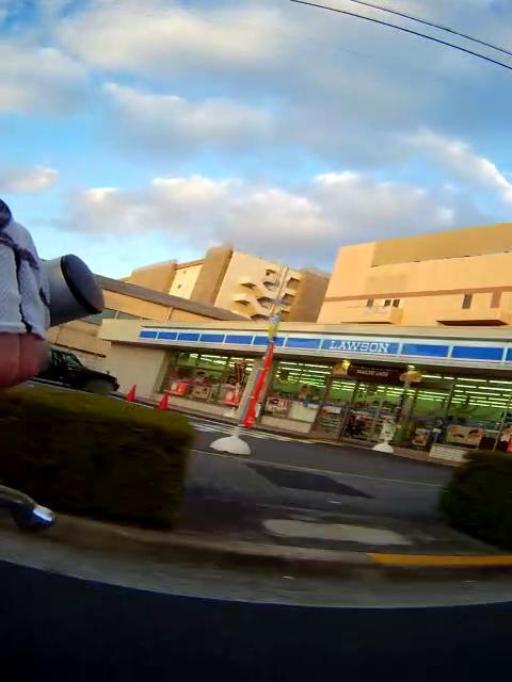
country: JP
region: Osaka
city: Osaka-shi
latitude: 34.7212
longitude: 135.4769
